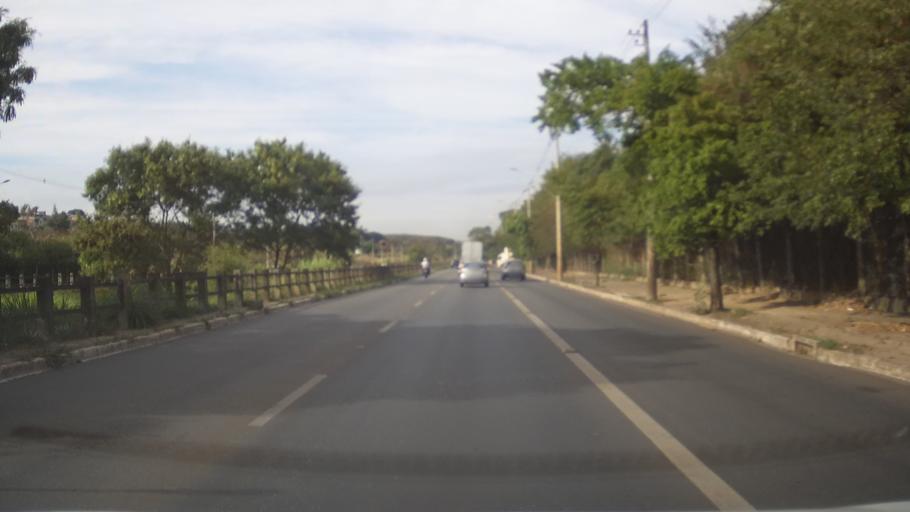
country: BR
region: Minas Gerais
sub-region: Contagem
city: Contagem
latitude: -19.8899
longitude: -44.0387
